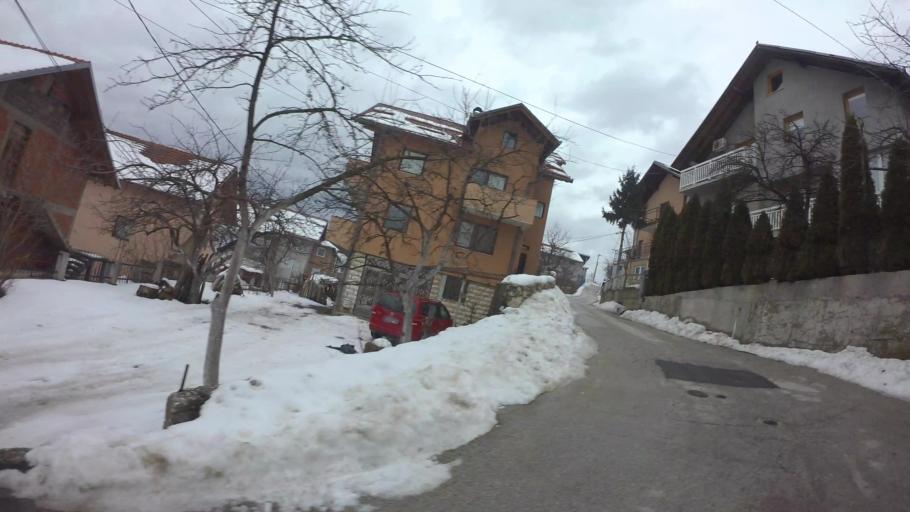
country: BA
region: Federation of Bosnia and Herzegovina
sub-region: Kanton Sarajevo
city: Sarajevo
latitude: 43.8643
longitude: 18.3206
